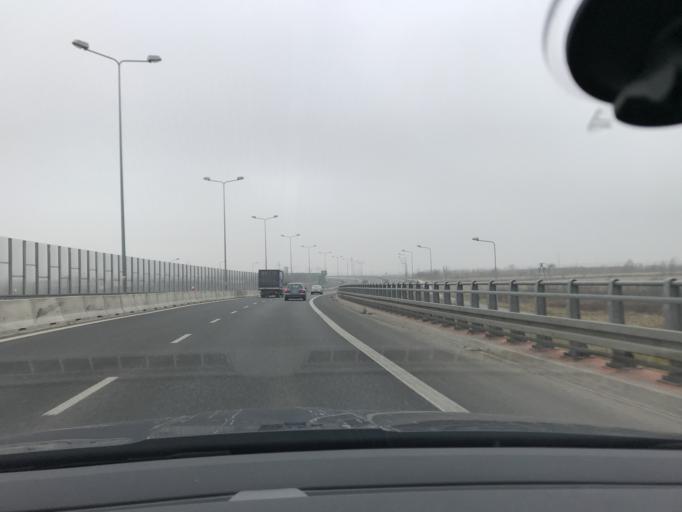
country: PL
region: Lodz Voivodeship
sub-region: Powiat pabianicki
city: Ksawerow
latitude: 51.6987
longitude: 19.4114
